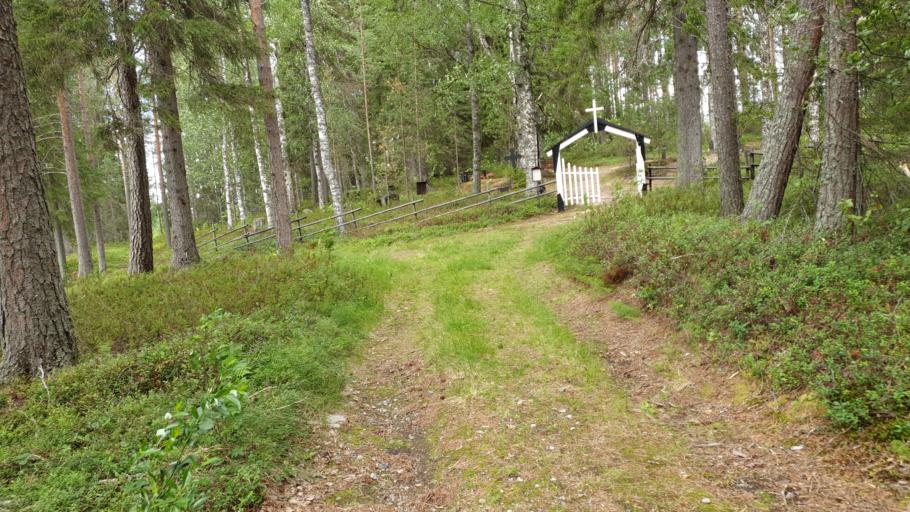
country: FI
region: Kainuu
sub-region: Kehys-Kainuu
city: Kuhmo
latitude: 64.3824
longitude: 29.8026
